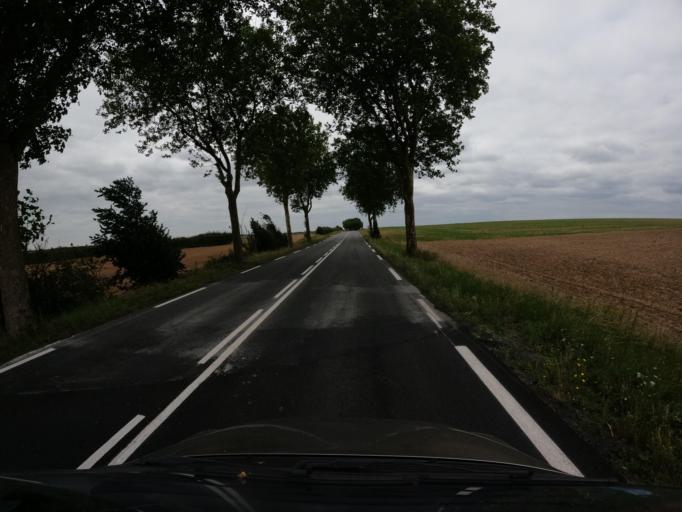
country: FR
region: Pays de la Loire
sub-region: Departement de la Vendee
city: Saint-Martin-sous-Mouzeuil
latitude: 46.5178
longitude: -0.9762
